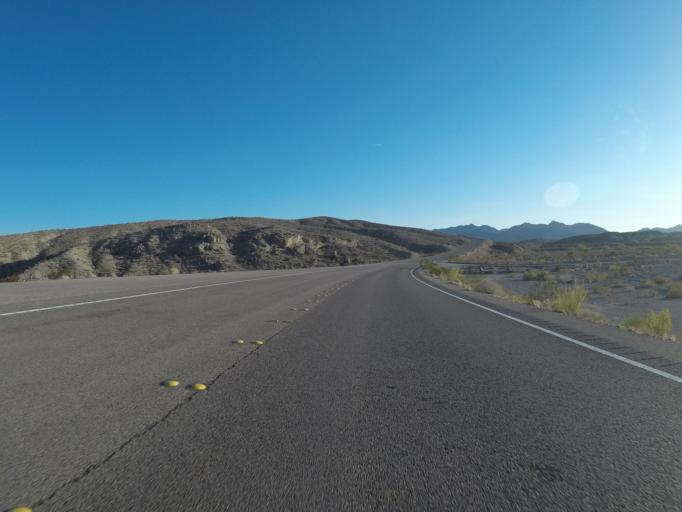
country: US
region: Nevada
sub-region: Clark County
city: Moapa Valley
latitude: 36.3082
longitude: -114.4892
